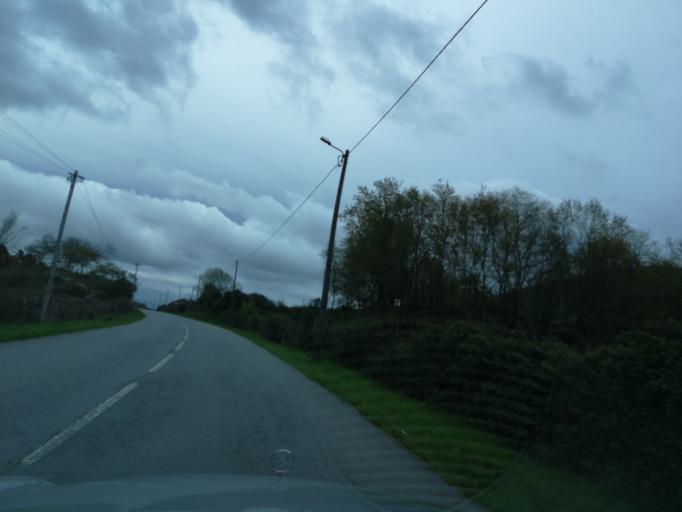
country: PT
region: Braga
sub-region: Braga
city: Oliveira
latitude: 41.4811
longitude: -8.4562
